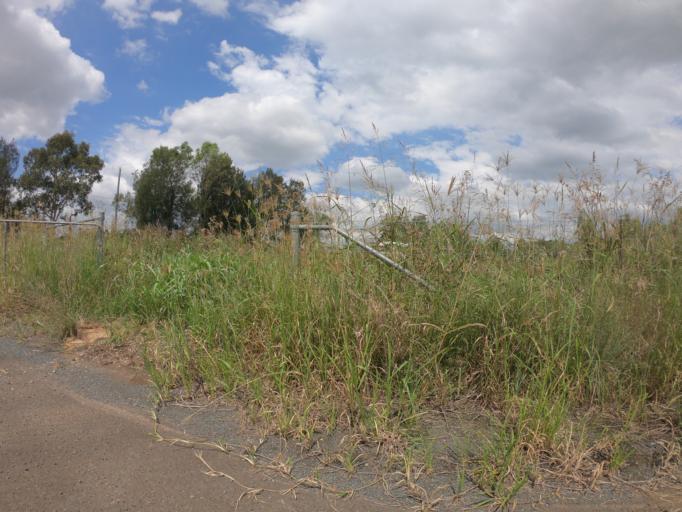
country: AU
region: New South Wales
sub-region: Blacktown
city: Mount Druitt
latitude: -33.8024
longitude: 150.7683
